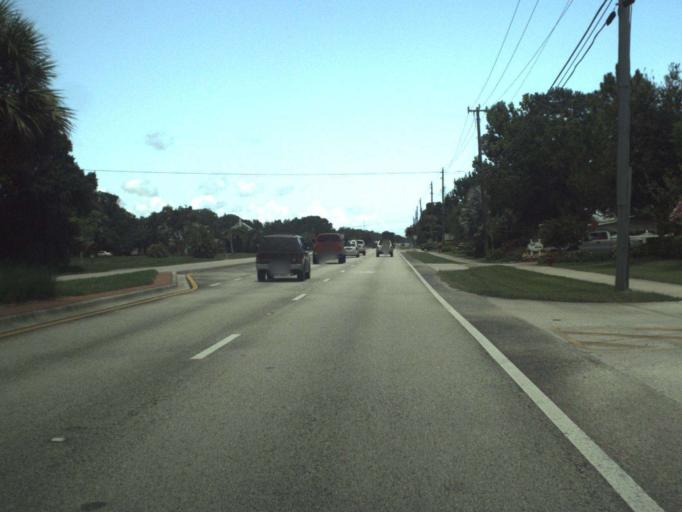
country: US
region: Florida
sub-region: Indian River County
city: Wabasso Beach
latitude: 27.7572
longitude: -80.4382
